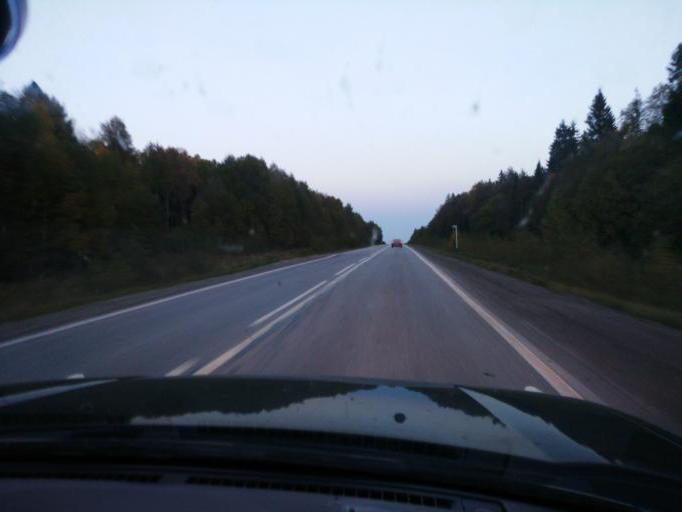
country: RU
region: Perm
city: Verkhnechusovskiye Gorodki
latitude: 58.2626
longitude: 56.9725
